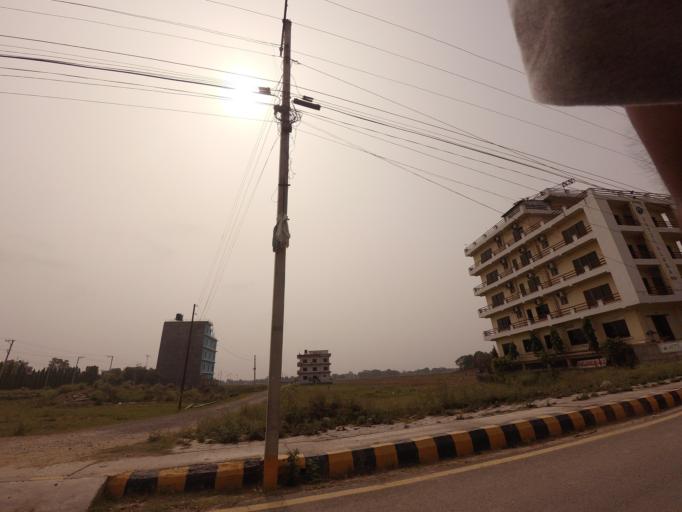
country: IN
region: Uttar Pradesh
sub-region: Maharajganj
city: Nautanwa
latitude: 27.4675
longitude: 83.2838
